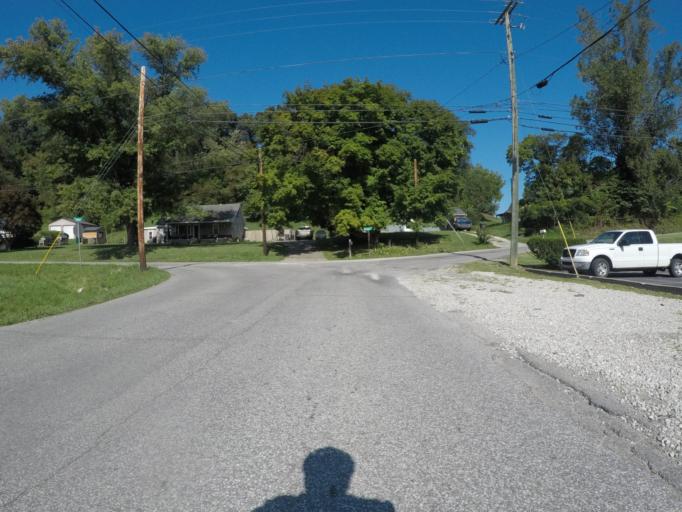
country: US
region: Kentucky
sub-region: Boyd County
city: Westwood
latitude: 38.4845
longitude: -82.6638
